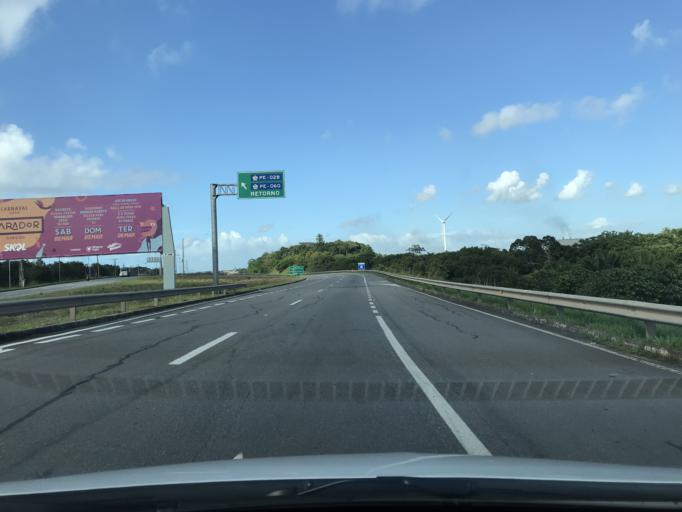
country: BR
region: Pernambuco
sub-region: Cabo De Santo Agostinho
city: Cabo
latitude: -8.3209
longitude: -34.9992
